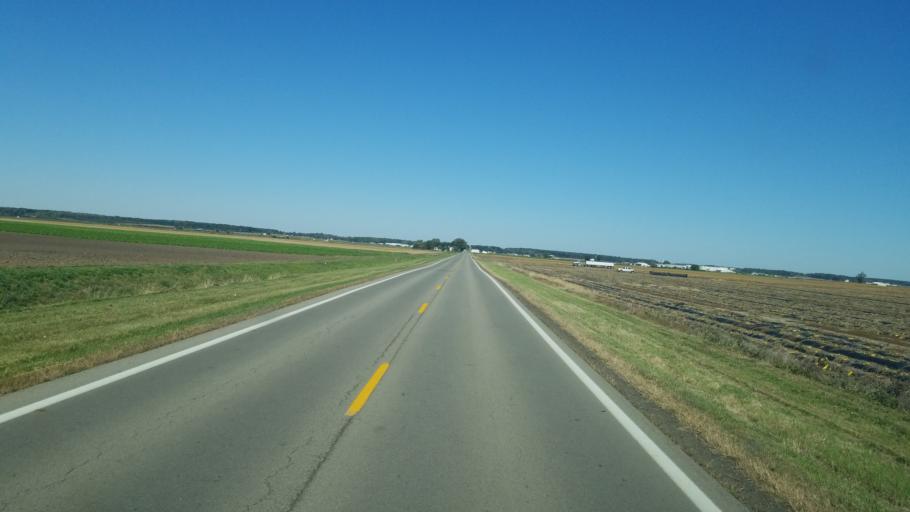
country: US
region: Ohio
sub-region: Huron County
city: Willard
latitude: 40.9987
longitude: -82.7297
